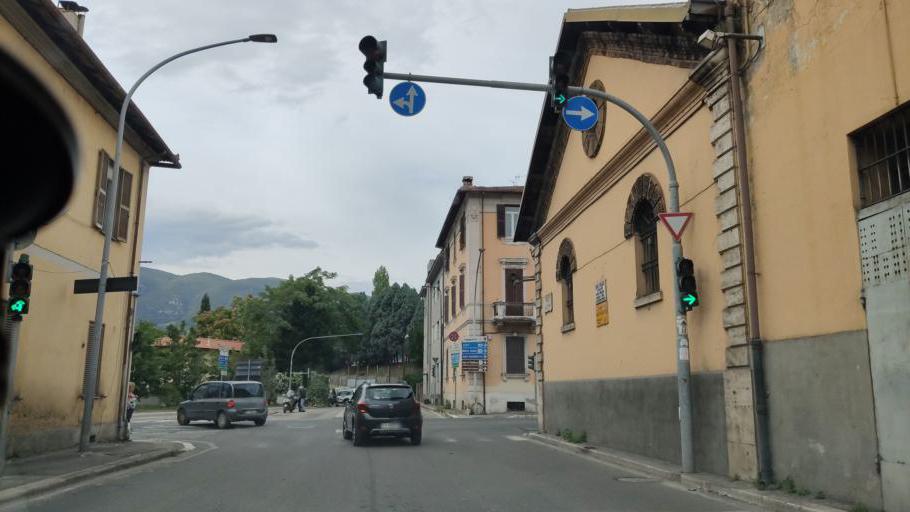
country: IT
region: Umbria
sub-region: Provincia di Terni
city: Terni
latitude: 42.5640
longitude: 12.6588
